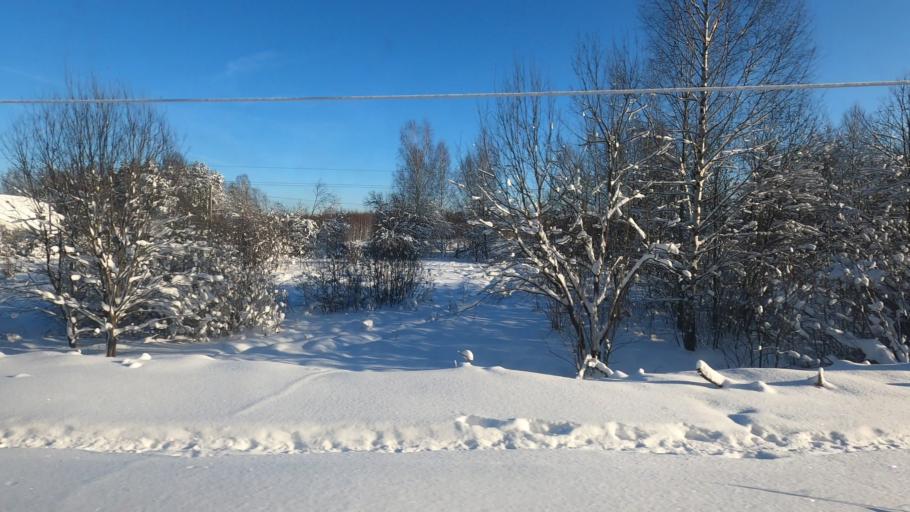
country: RU
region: Moskovskaya
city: Novo-Nikol'skoye
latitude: 56.6421
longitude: 37.5621
